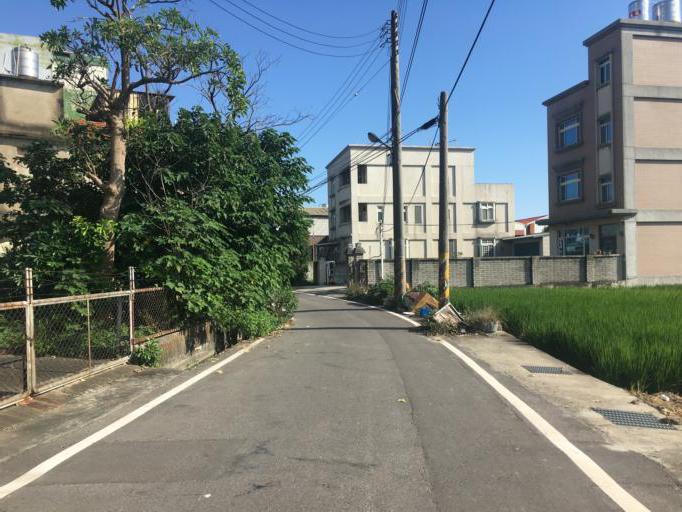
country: TW
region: Taiwan
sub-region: Hsinchu
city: Zhubei
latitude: 24.8411
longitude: 120.9868
